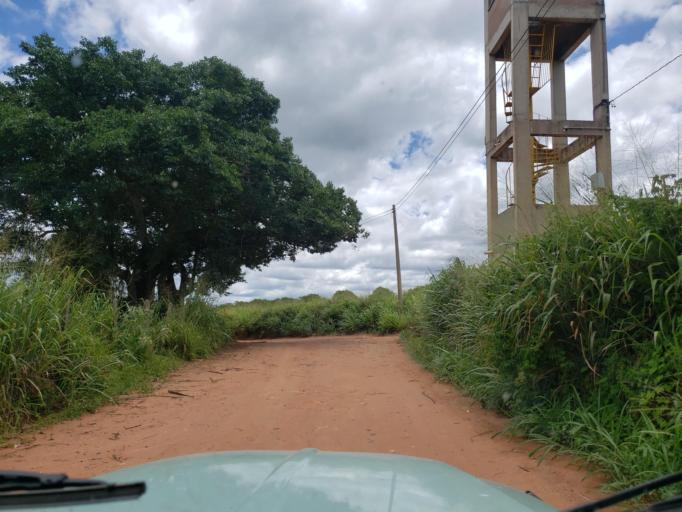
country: BR
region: Sao Paulo
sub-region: Santo Antonio Do Jardim
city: Espirito Santo do Pinhal
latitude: -22.2174
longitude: -46.8371
